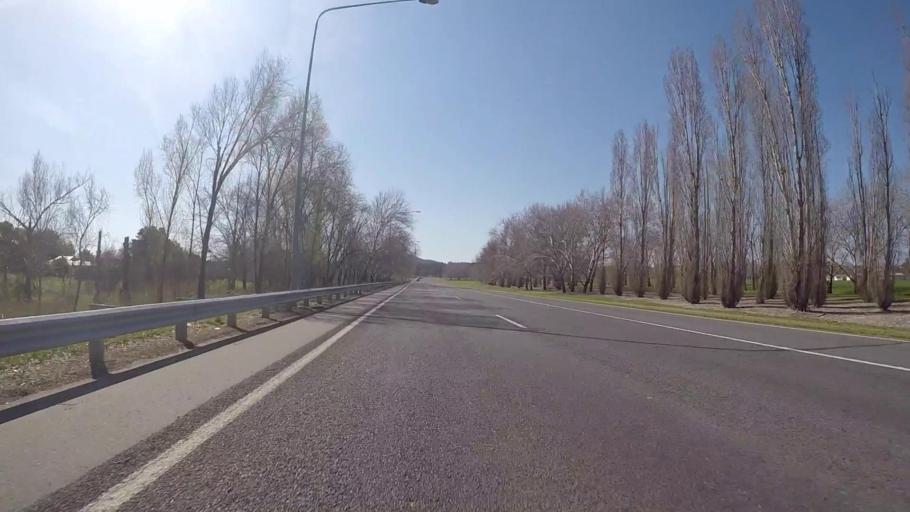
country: AU
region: Australian Capital Territory
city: Forrest
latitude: -35.3219
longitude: 149.0885
